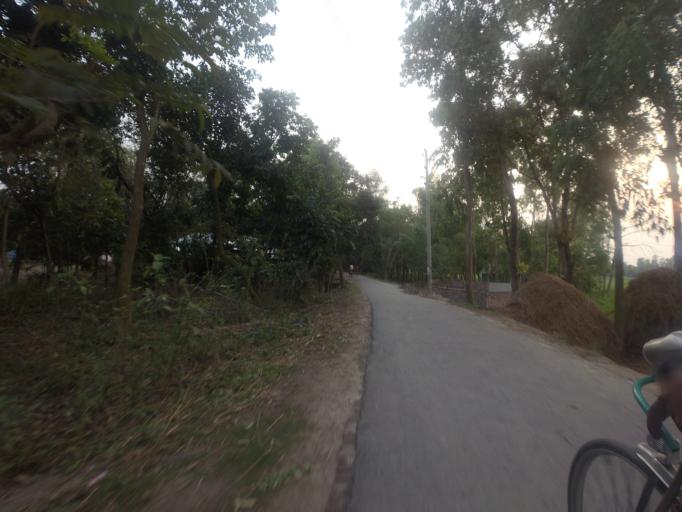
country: BD
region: Rajshahi
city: Sirajganj
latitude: 24.3298
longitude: 89.6789
